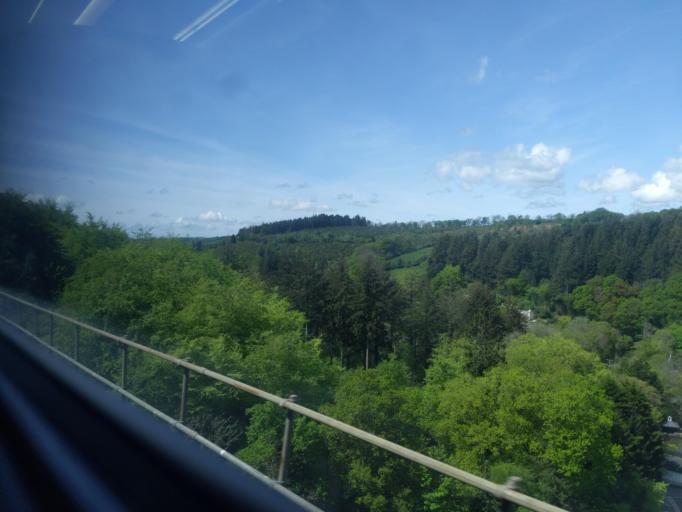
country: GB
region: England
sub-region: Cornwall
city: Liskeard
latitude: 50.4530
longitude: -4.5682
